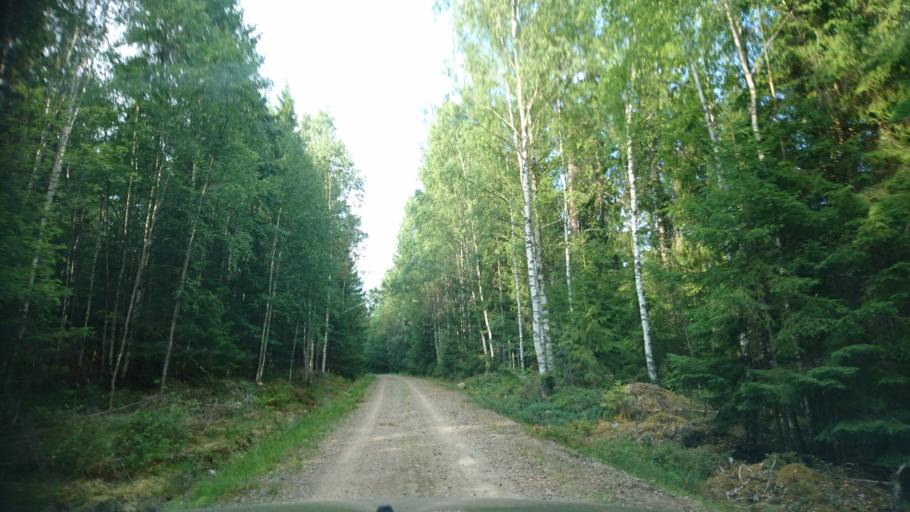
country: SE
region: Vaermland
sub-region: Kristinehamns Kommun
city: Bjorneborg
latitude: 59.3045
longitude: 14.3109
